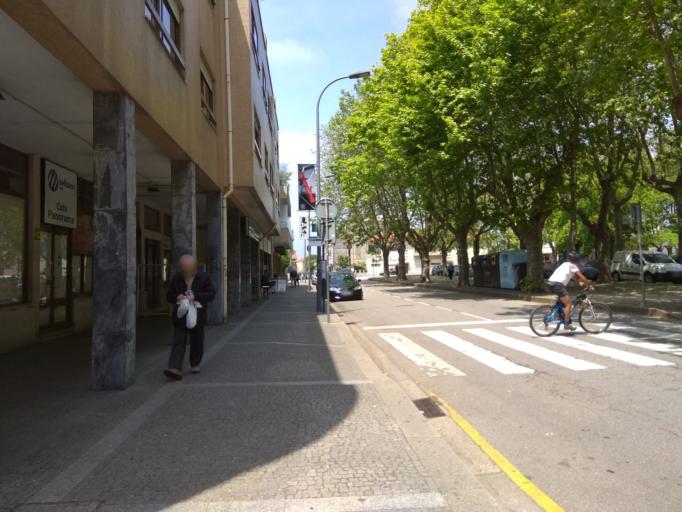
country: PT
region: Porto
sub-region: Matosinhos
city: Matosinhos
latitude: 41.1824
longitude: -8.6844
